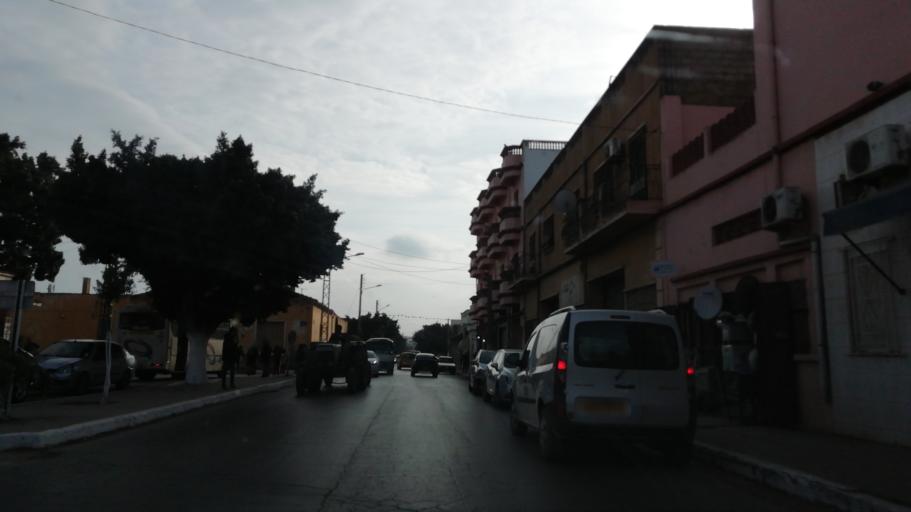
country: DZ
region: Mostaganem
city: Mostaganem
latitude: 35.8634
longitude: 0.0741
